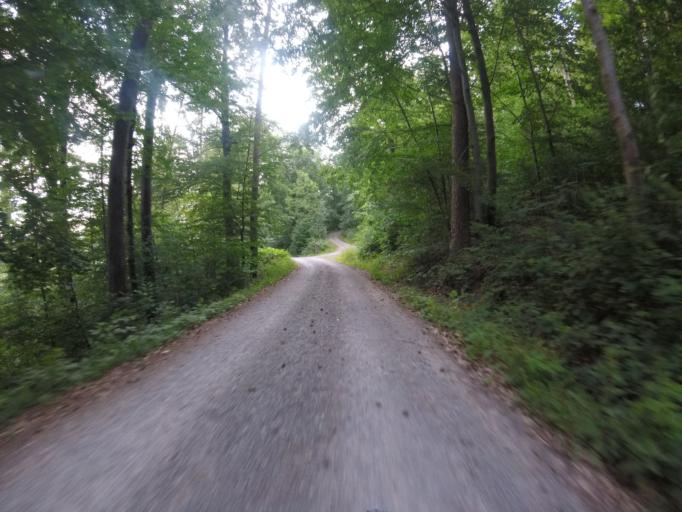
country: DE
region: Baden-Wuerttemberg
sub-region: Regierungsbezirk Stuttgart
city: Oppenweiler
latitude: 48.9682
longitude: 9.4910
